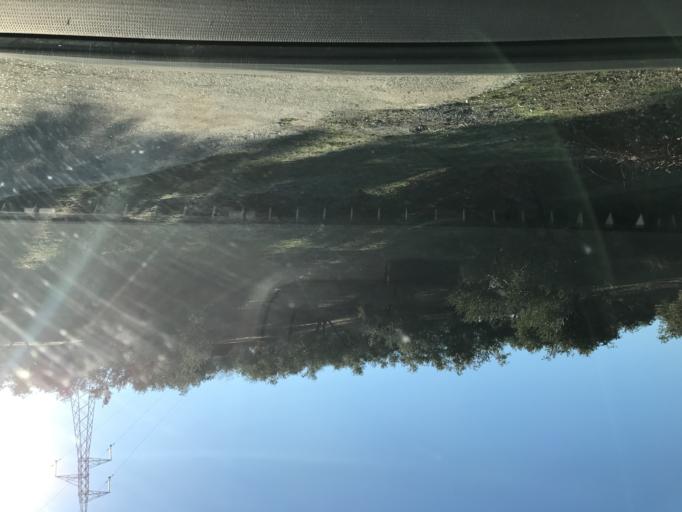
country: ES
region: Andalusia
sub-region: Provincia de Granada
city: Peligros
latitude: 37.2442
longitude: -3.6353
